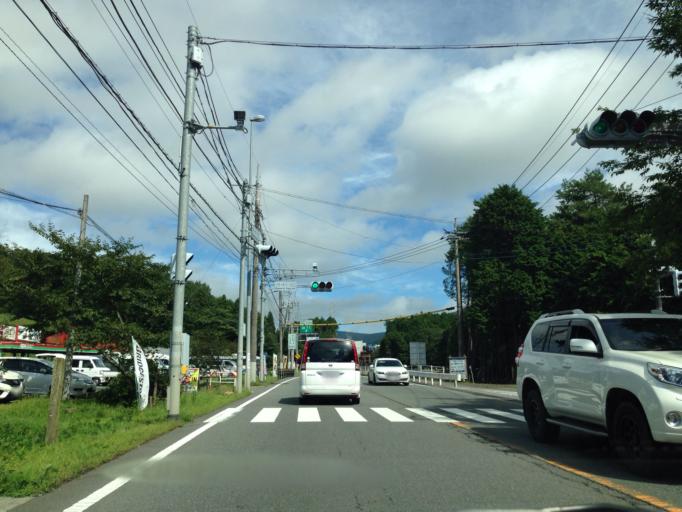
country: JP
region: Shizuoka
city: Gotemba
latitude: 35.3476
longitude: 138.8789
